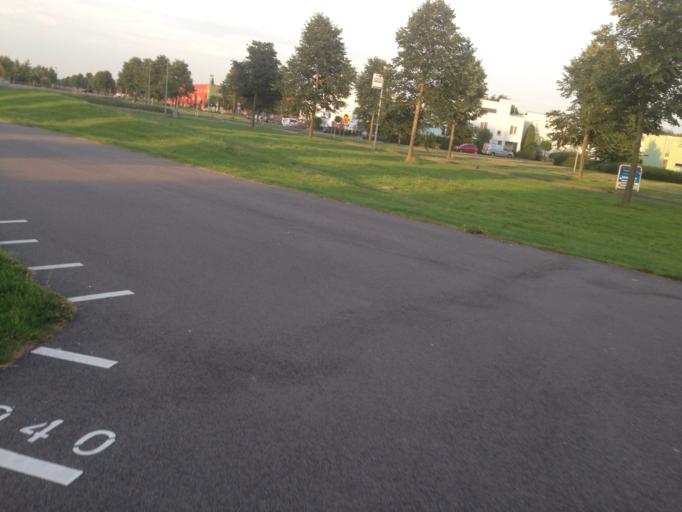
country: NL
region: Flevoland
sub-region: Gemeente Almere
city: Almere Stad
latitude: 52.3966
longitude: 5.2901
